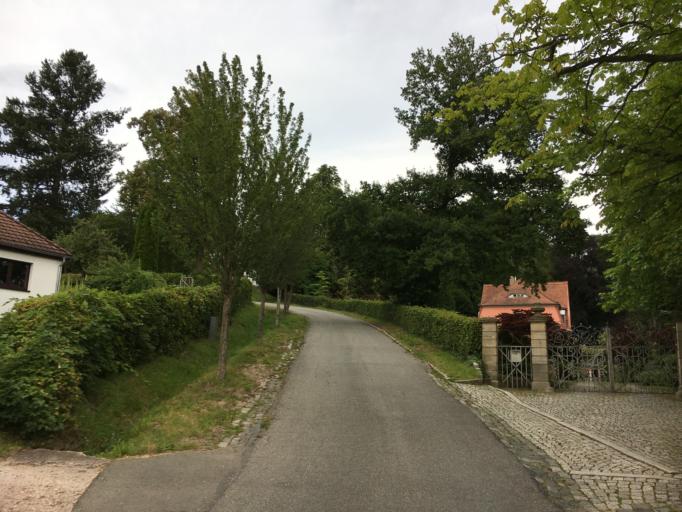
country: DE
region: Thuringia
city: Schmalkalden
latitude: 50.7233
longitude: 10.4569
